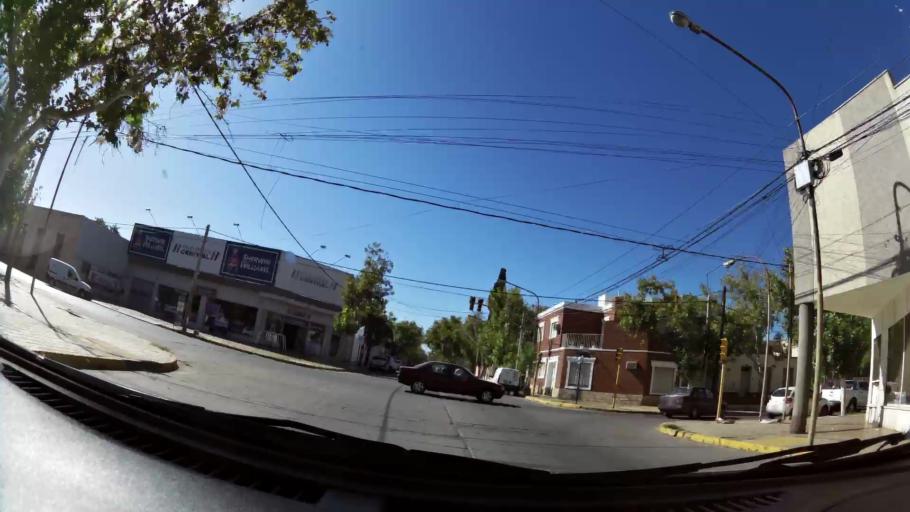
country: AR
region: San Juan
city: San Juan
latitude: -31.5424
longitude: -68.5344
